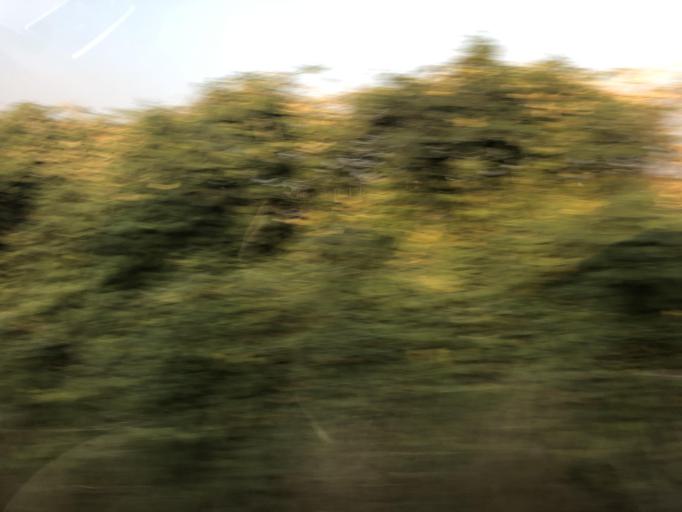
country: TW
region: Taiwan
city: Xinying
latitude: 23.1594
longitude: 120.2714
